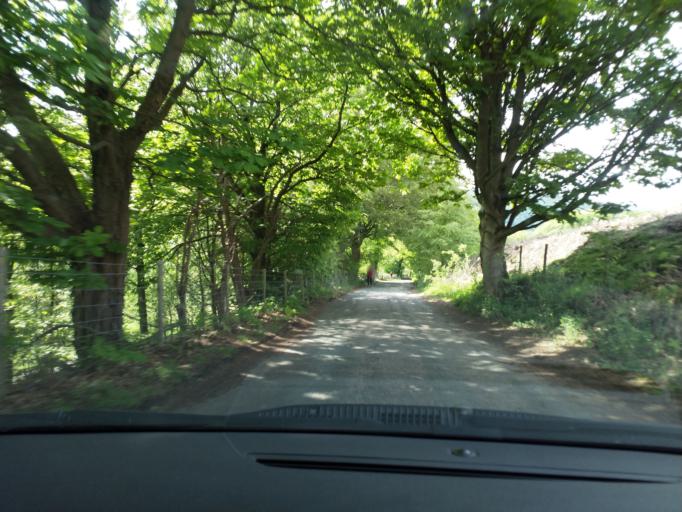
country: GB
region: England
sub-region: Derbyshire
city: Hathersage
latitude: 53.3564
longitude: -1.6918
